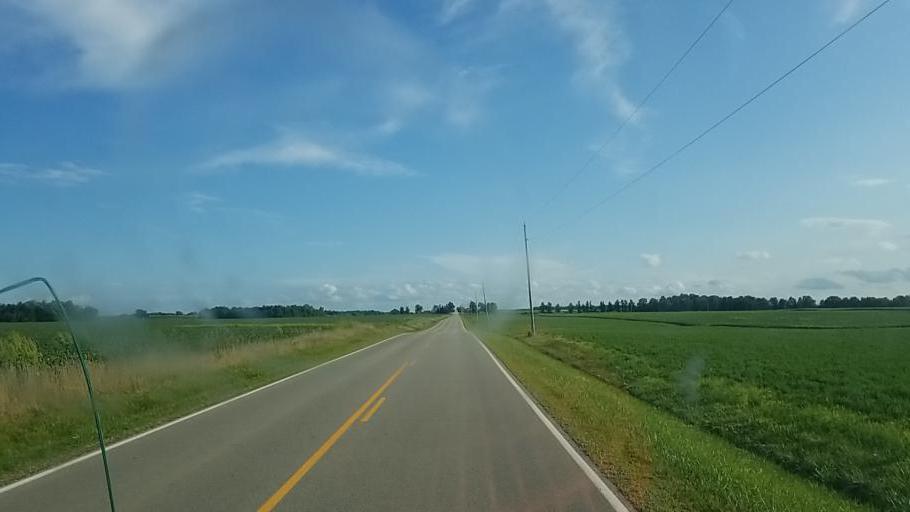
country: US
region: Ohio
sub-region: Crawford County
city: Bucyrus
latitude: 40.8330
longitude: -83.0933
